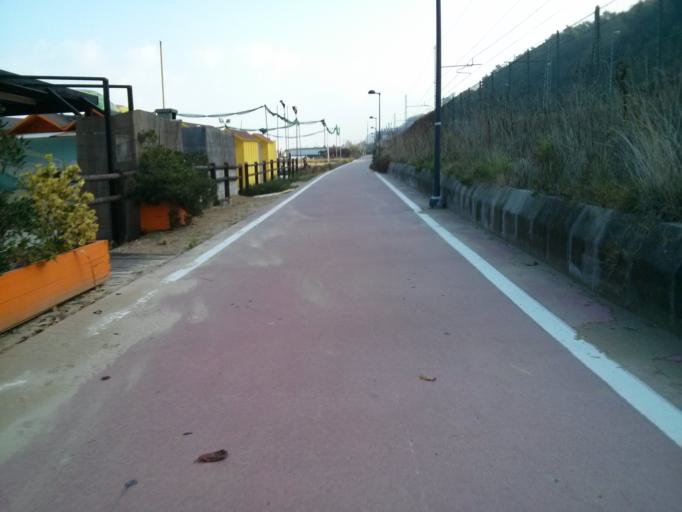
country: IT
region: The Marches
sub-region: Provincia di Pesaro e Urbino
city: Fenile
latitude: 43.8906
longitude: 12.9496
